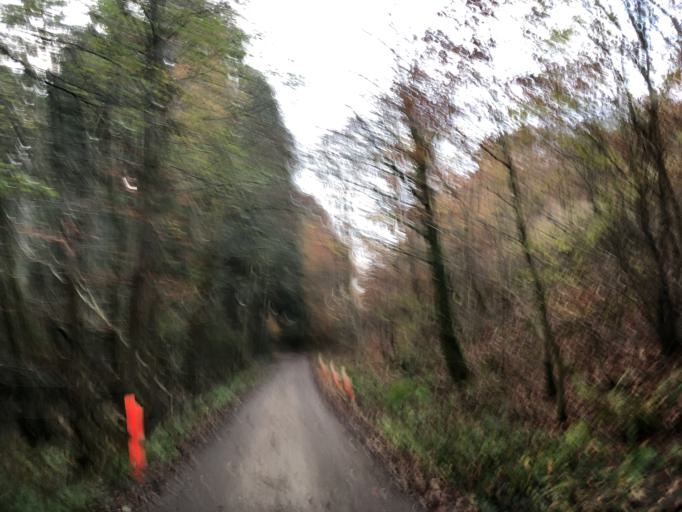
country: DK
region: Central Jutland
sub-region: Silkeborg Kommune
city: Silkeborg
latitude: 56.1428
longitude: 9.4823
